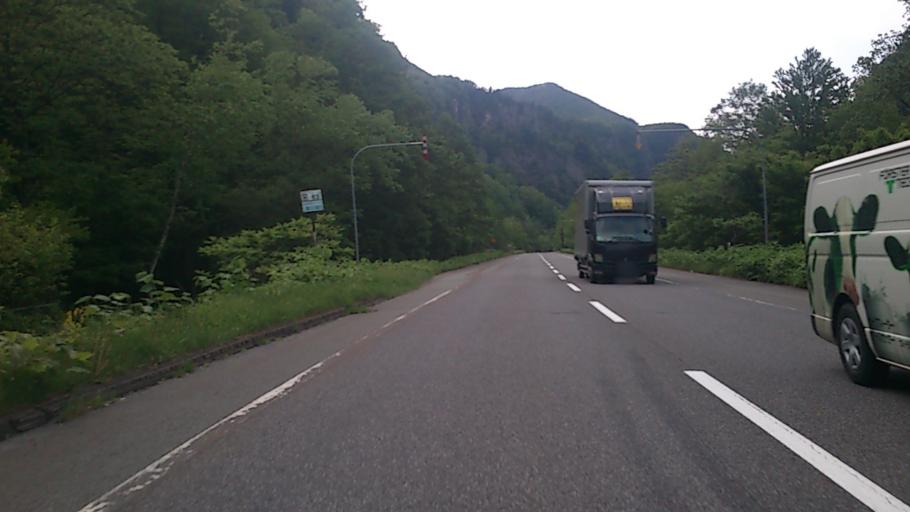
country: JP
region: Hokkaido
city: Kamikawa
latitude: 43.7560
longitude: 142.9261
